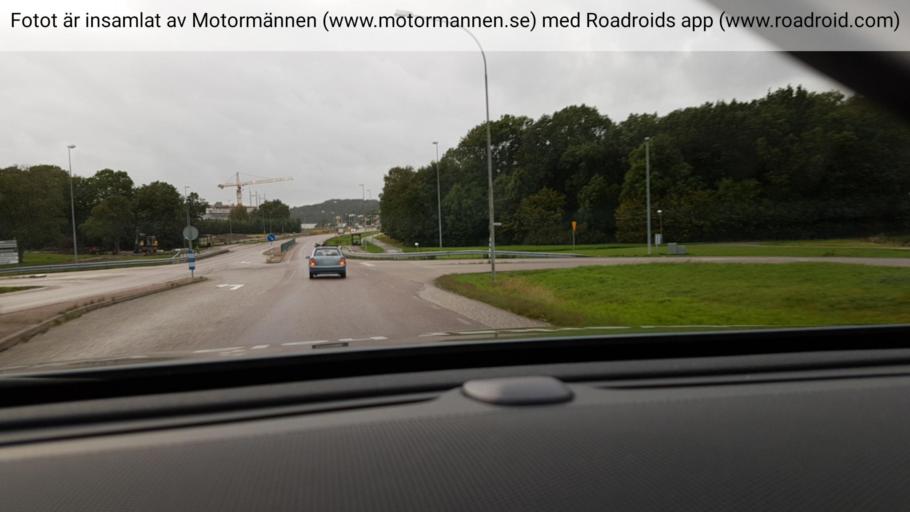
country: SE
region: Vaestra Goetaland
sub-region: Stenungsunds Kommun
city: Stenungsund
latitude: 58.0579
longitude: 11.8291
